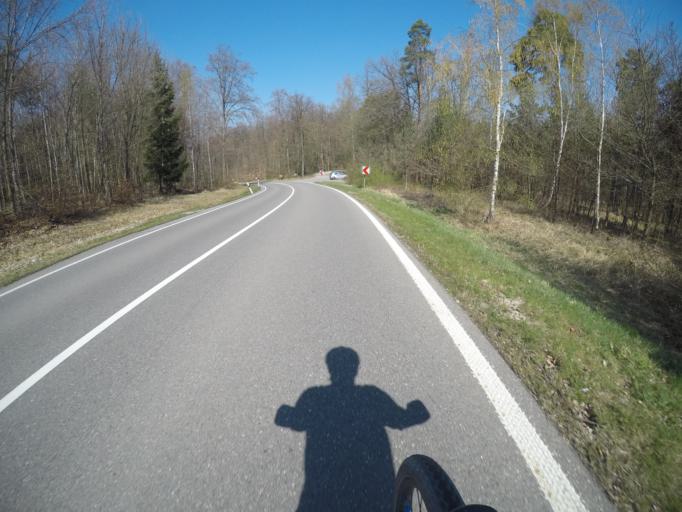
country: DE
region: Baden-Wuerttemberg
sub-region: Regierungsbezirk Stuttgart
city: Leonberg
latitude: 48.7596
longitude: 9.0127
